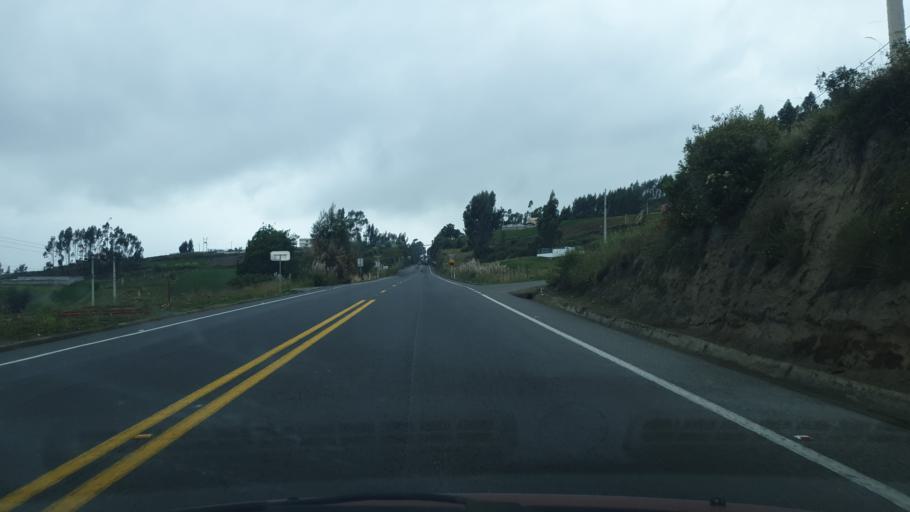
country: EC
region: Tungurahua
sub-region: Canton Quero
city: Quero
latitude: -1.3723
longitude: -78.6515
